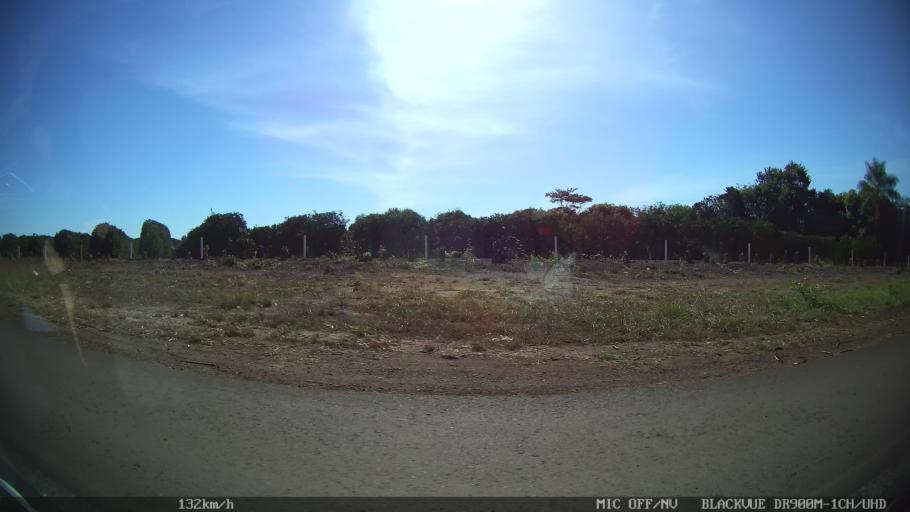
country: BR
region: Sao Paulo
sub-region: Barretos
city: Barretos
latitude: -20.5888
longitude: -48.7048
